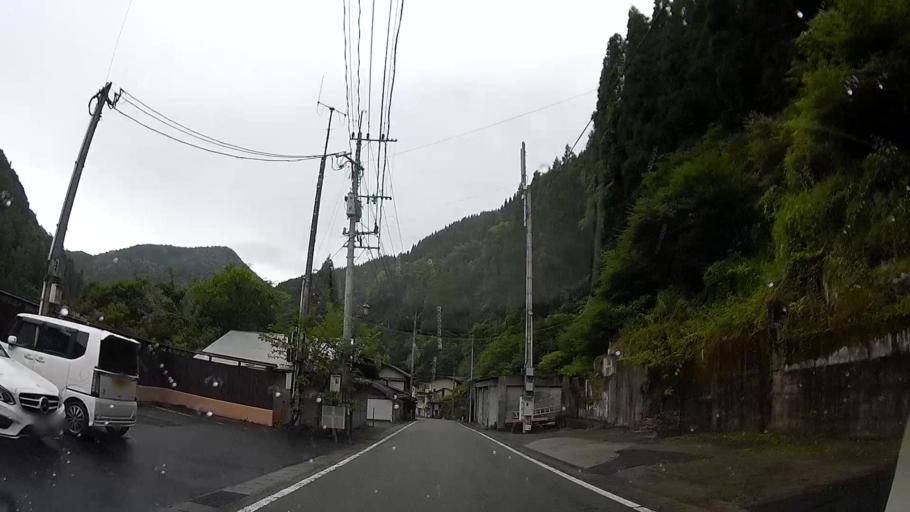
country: JP
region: Oita
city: Tsukawaki
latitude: 33.1787
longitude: 131.0376
